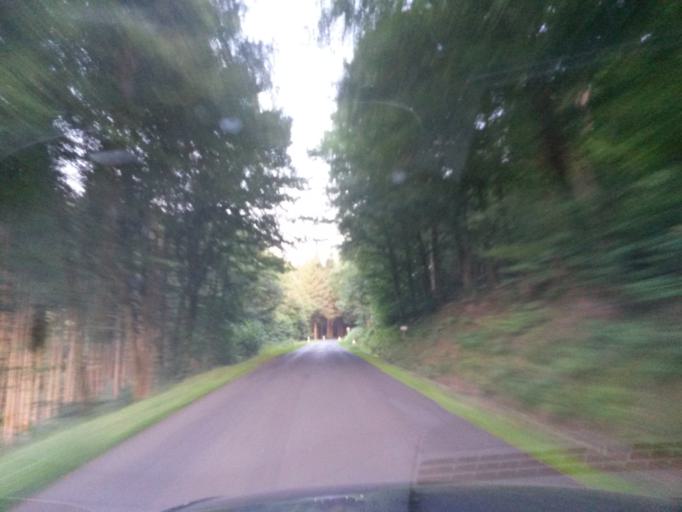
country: DE
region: Bavaria
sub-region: Regierungsbezirk Unterfranken
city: Neustadt am Main
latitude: 49.8993
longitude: 9.5510
